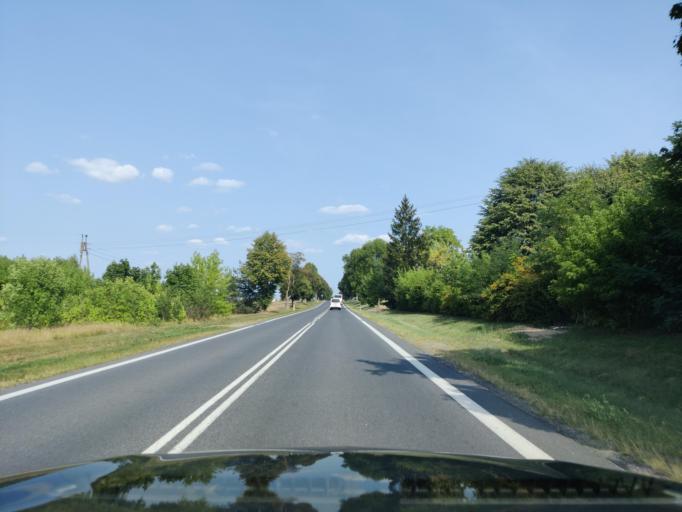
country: PL
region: Masovian Voivodeship
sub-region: Powiat makowski
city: Szelkow
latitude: 52.8406
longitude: 21.2589
